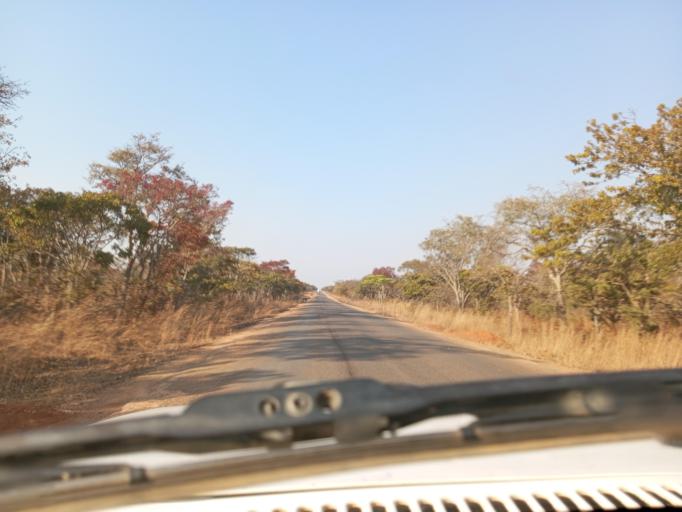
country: ZM
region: Northern
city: Mpika
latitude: -12.3995
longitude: 31.0893
